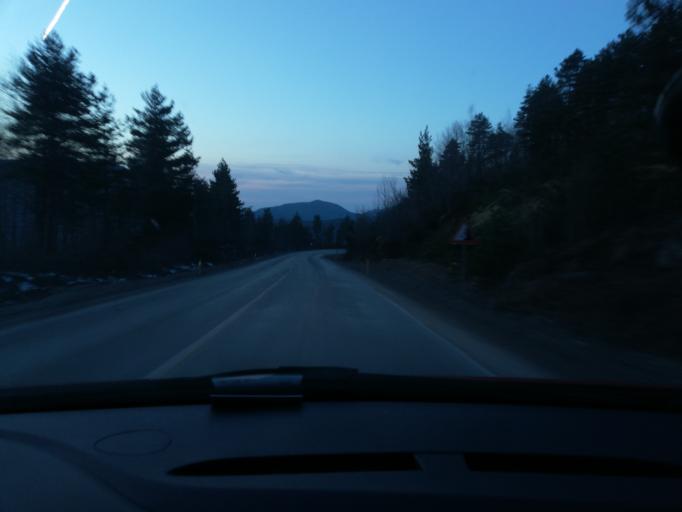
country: TR
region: Kastamonu
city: Kure
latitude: 41.8948
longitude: 33.7072
